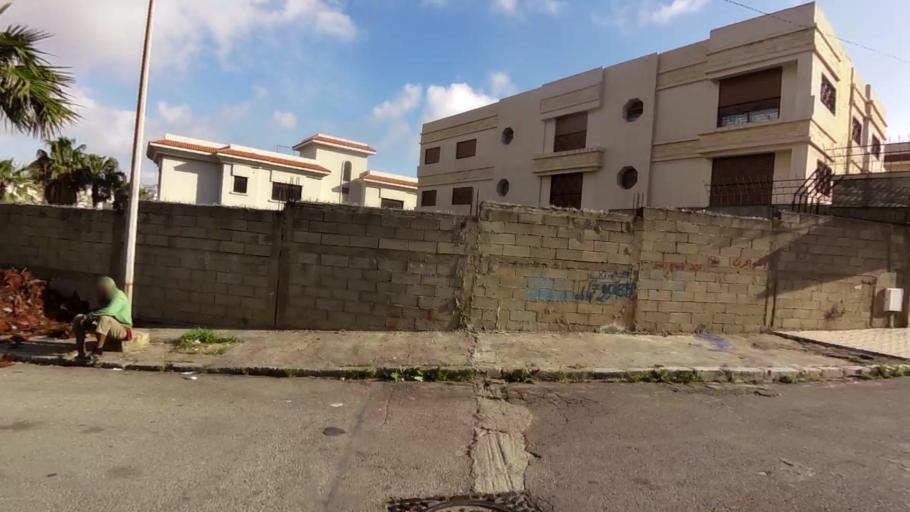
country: MA
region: Tanger-Tetouan
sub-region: Tanger-Assilah
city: Tangier
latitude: 35.7683
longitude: -5.7994
